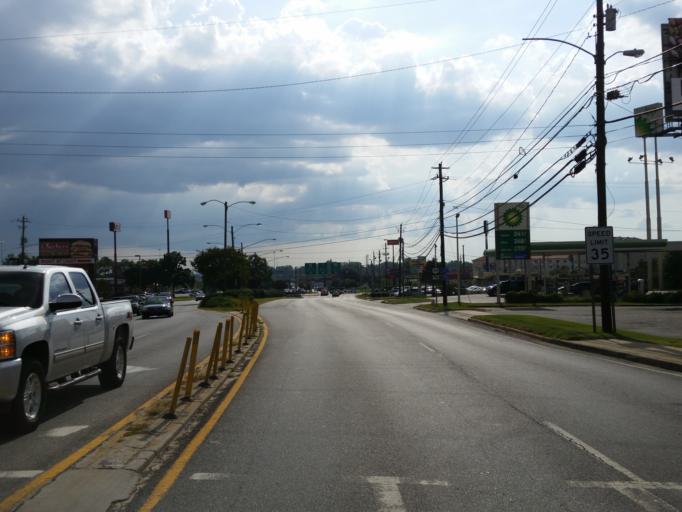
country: US
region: Georgia
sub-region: Tift County
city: Tifton
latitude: 31.4508
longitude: -83.5255
